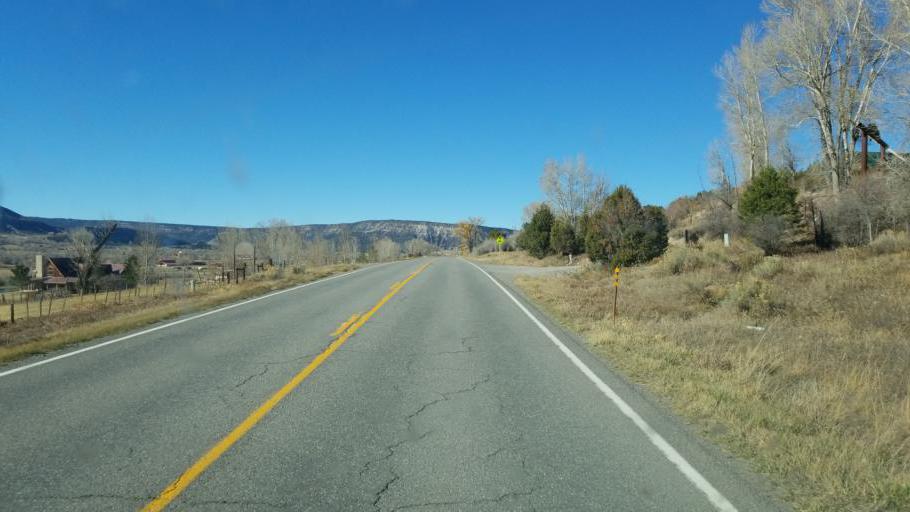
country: US
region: Colorado
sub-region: Ouray County
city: Ouray
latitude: 38.1295
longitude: -107.7313
